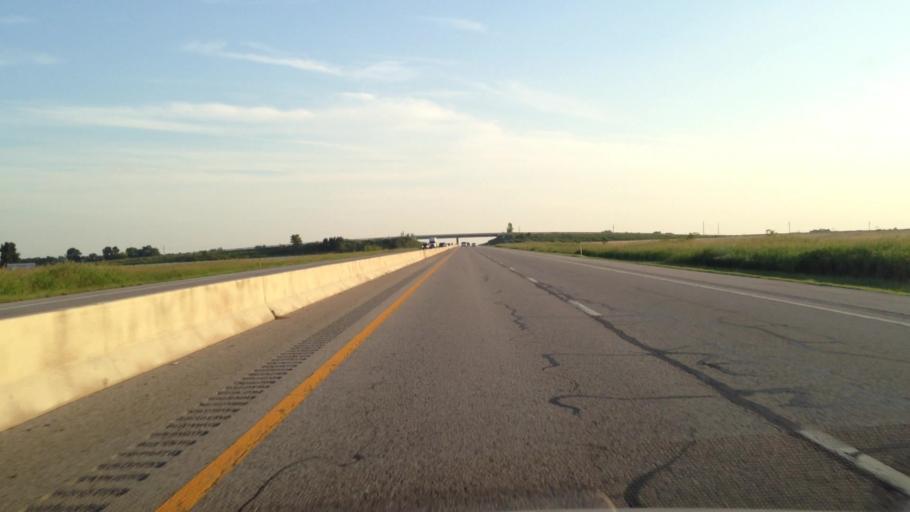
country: US
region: Oklahoma
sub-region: Ottawa County
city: Fairland
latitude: 36.8064
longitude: -94.8778
